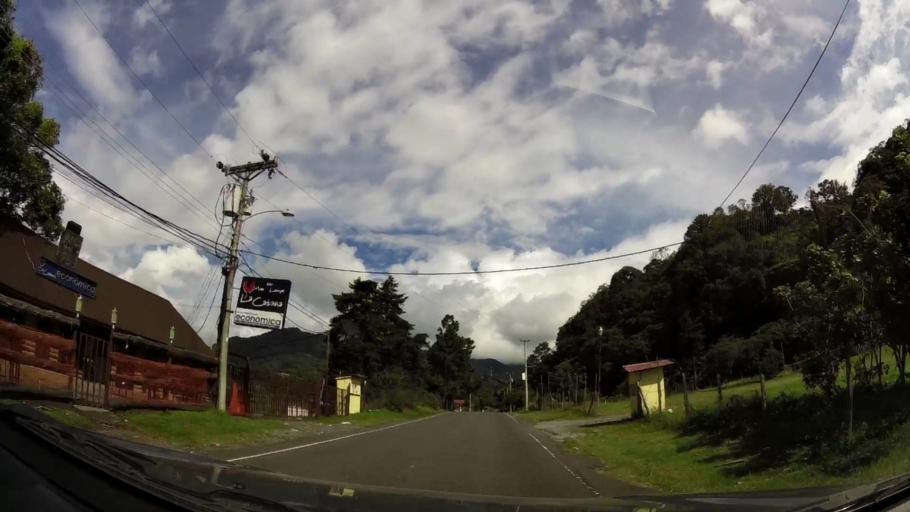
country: PA
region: Chiriqui
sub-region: Distrito Boquete
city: Boquete
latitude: 8.7794
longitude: -82.4299
